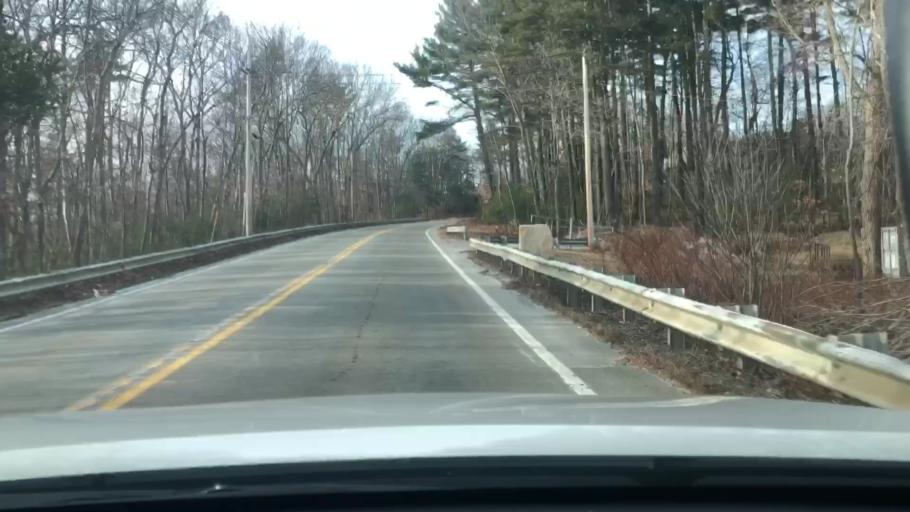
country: US
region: Massachusetts
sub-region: Worcester County
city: Upton
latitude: 42.1555
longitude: -71.5777
